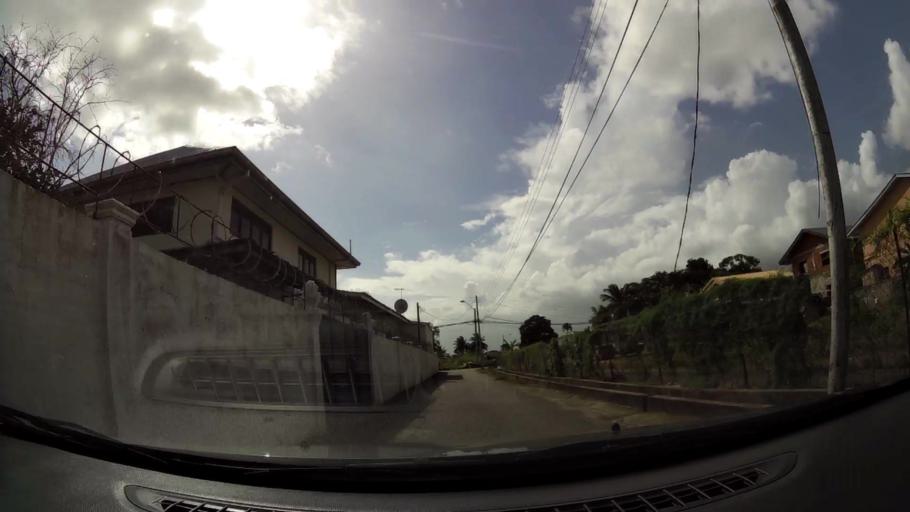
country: TT
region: Tunapuna/Piarco
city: Arouca
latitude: 10.6188
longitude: -61.3257
